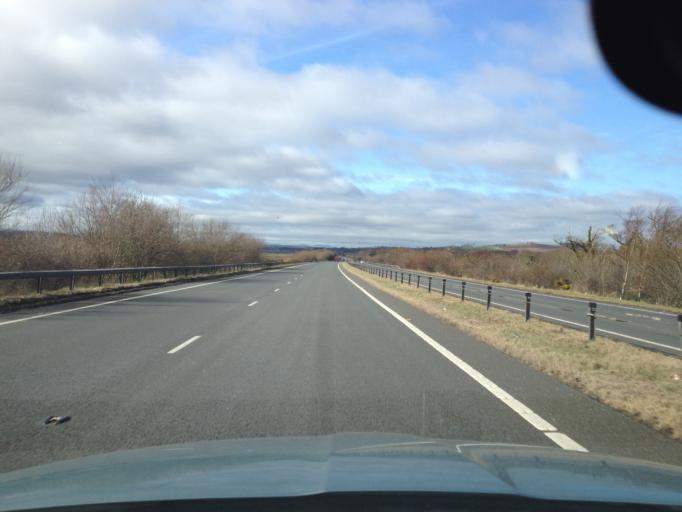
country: GB
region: Scotland
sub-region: East Lothian
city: East Linton
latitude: 55.9743
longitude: -2.7084
